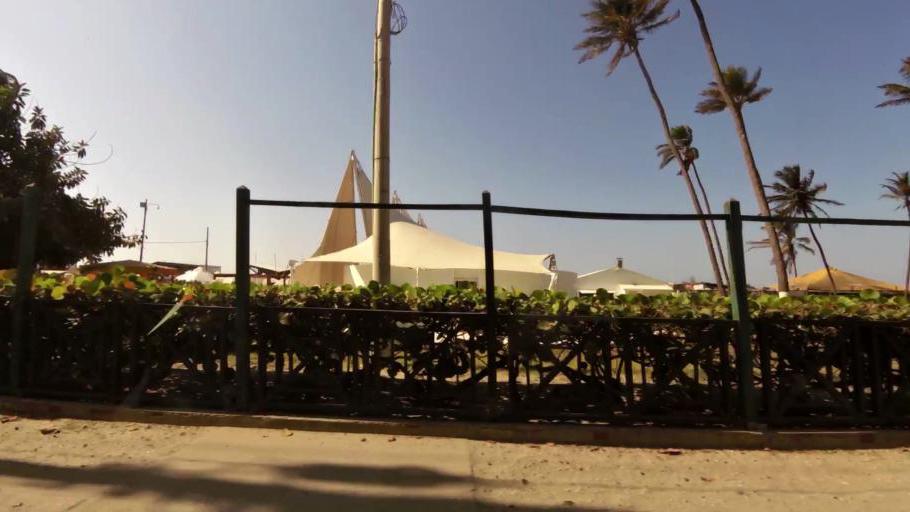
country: CO
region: Bolivar
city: Cartagena
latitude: 10.3981
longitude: -75.5621
